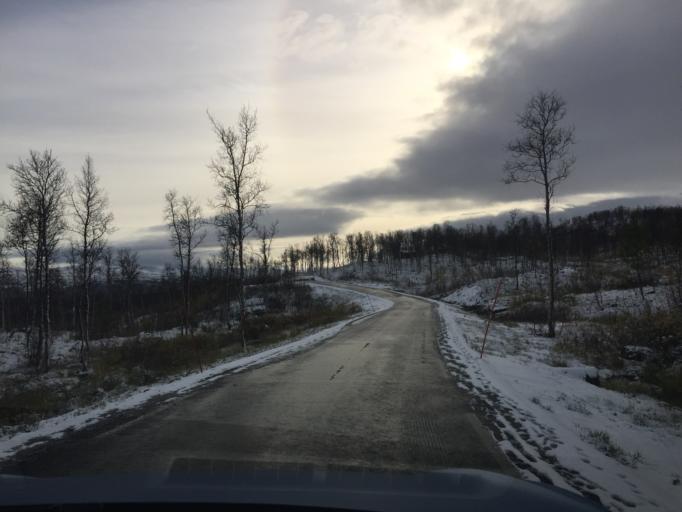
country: NO
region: Nordland
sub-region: Sorfold
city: Straumen
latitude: 67.0883
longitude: 16.0208
